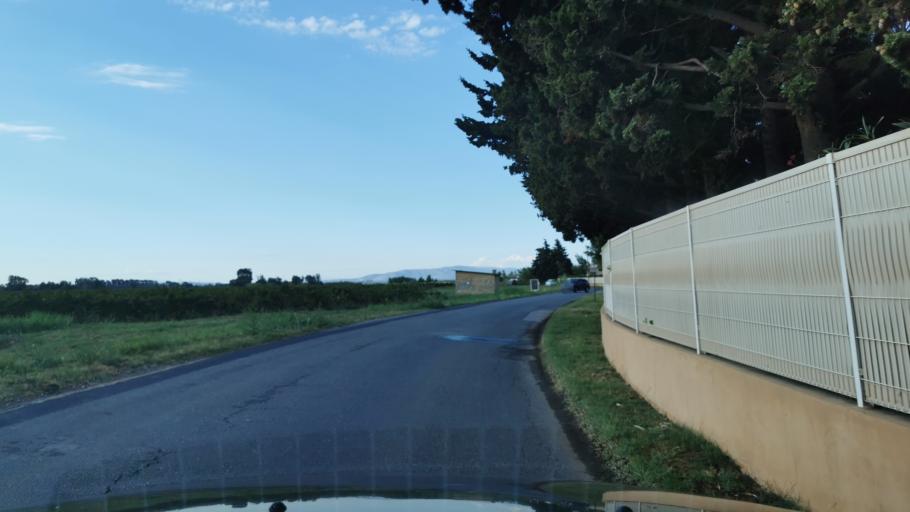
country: FR
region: Languedoc-Roussillon
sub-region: Departement de l'Aude
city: Narbonne
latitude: 43.1371
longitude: 3.0267
